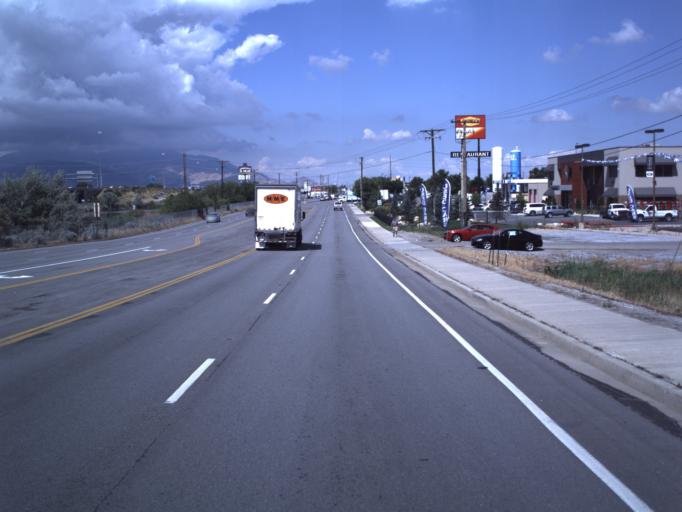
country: US
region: Utah
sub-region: Salt Lake County
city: South Salt Lake
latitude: 40.7256
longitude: -111.9115
